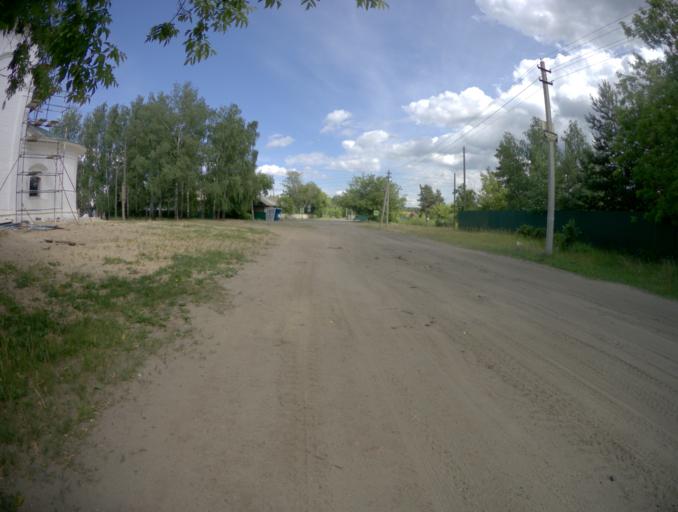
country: RU
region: Nizjnij Novgorod
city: Frolishchi
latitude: 56.4212
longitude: 42.6452
